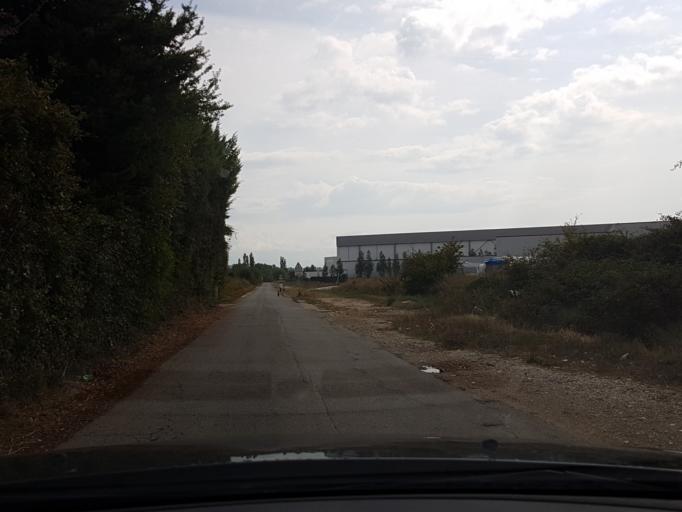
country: FR
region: Provence-Alpes-Cote d'Azur
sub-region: Departement du Vaucluse
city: Entraigues-sur-la-Sorgue
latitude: 43.9867
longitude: 4.9308
